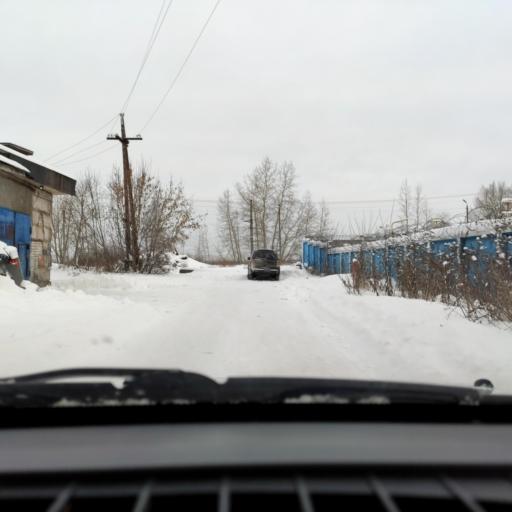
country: RU
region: Perm
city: Kondratovo
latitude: 58.0089
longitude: 56.1217
